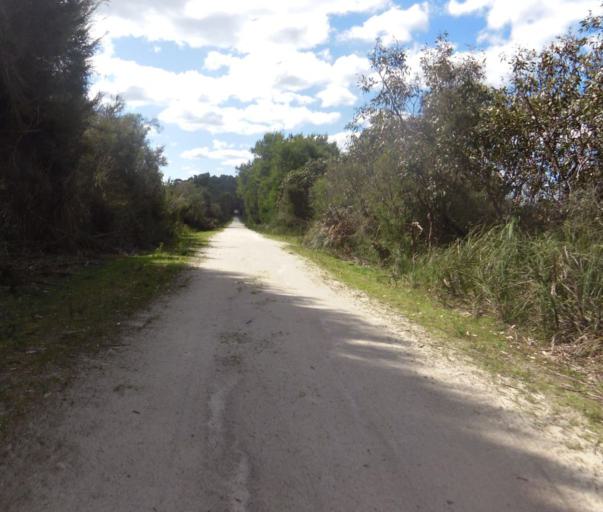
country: AU
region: Victoria
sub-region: Bass Coast
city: North Wonthaggi
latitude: -38.6130
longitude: 146.0434
